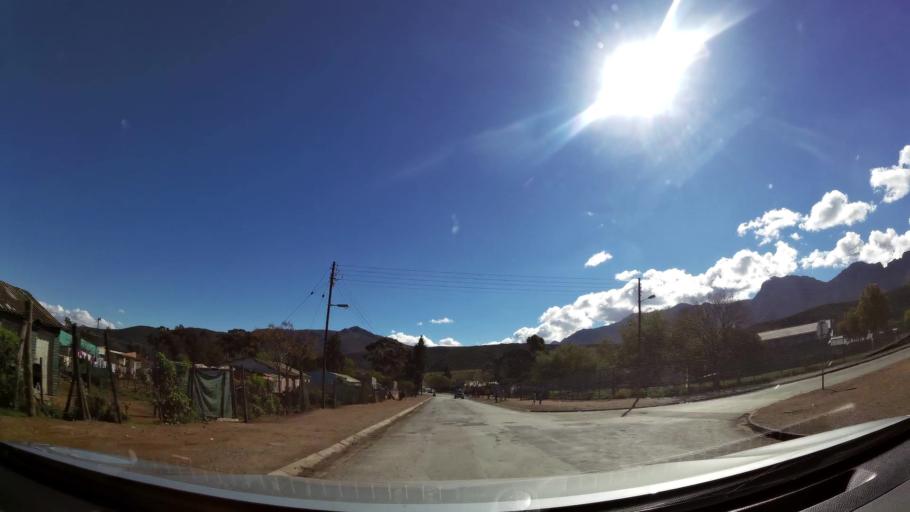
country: ZA
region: Western Cape
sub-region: Cape Winelands District Municipality
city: Ashton
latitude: -33.7891
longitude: 19.8899
